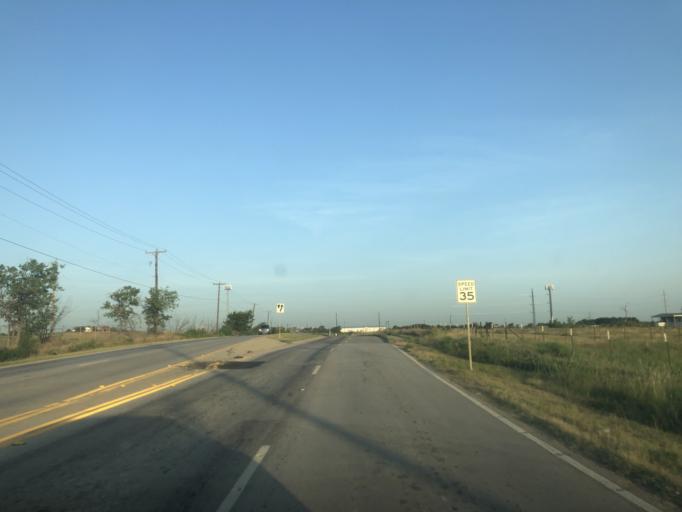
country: US
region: Texas
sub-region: Tarrant County
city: White Settlement
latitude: 32.7744
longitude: -97.4766
